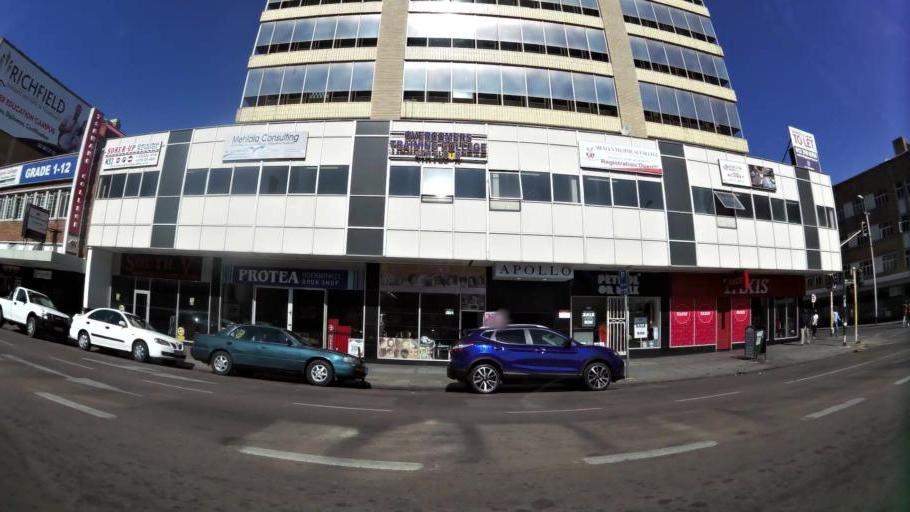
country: ZA
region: Gauteng
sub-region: City of Tshwane Metropolitan Municipality
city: Pretoria
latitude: -25.7456
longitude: 28.1981
